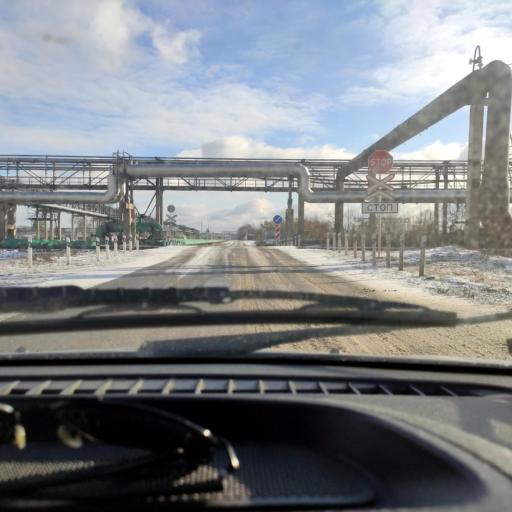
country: RU
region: Samara
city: Tol'yatti
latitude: 53.5365
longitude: 49.4678
